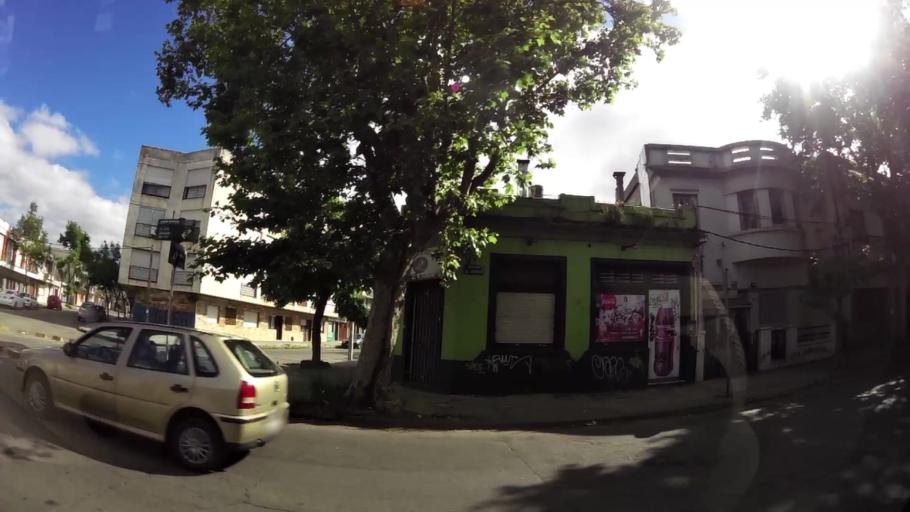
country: UY
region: Montevideo
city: Montevideo
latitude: -34.8777
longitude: -56.1760
